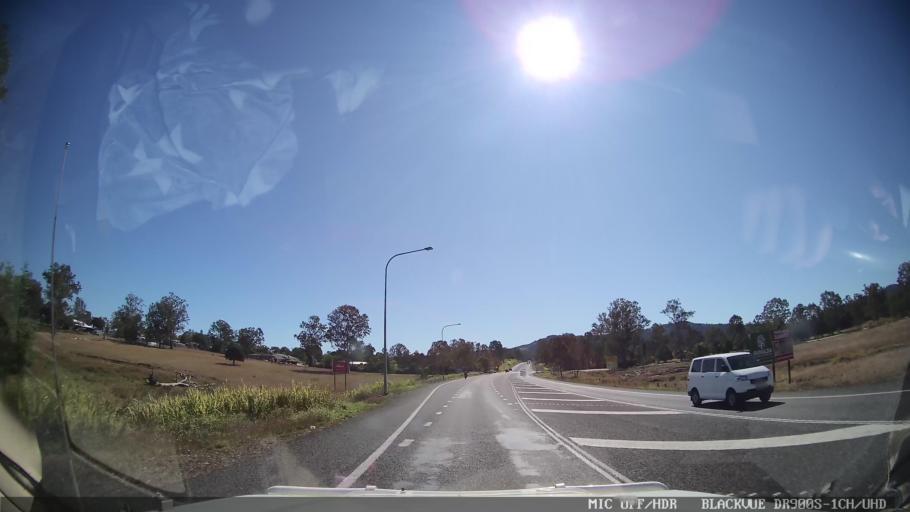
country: AU
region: Queensland
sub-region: Gympie Regional Council
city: Gympie
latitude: -25.9968
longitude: 152.5665
